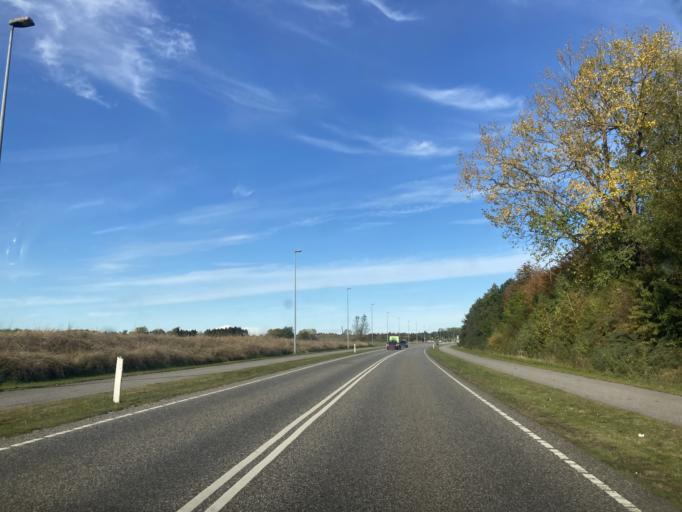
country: DK
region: Capital Region
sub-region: Vallensbaek Kommune
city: Vallensbaek
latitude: 55.6351
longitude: 12.3750
